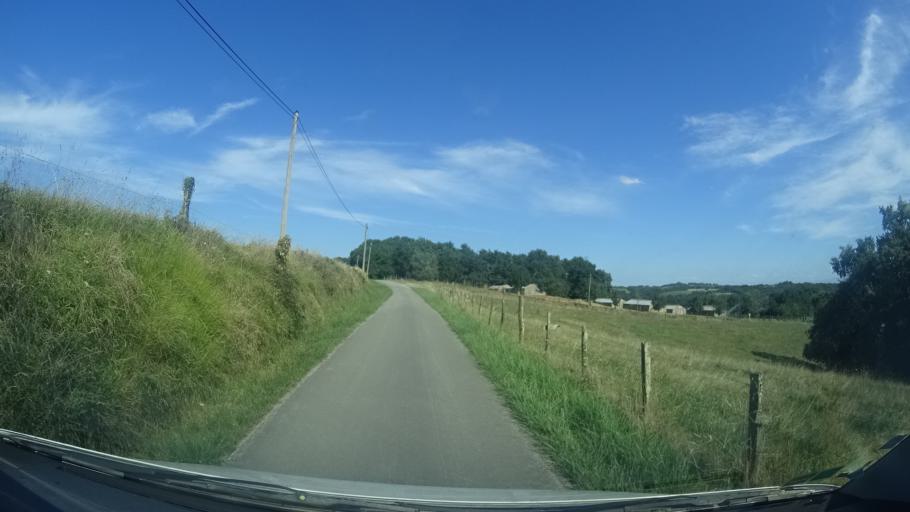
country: FR
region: Aquitaine
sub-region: Departement des Pyrenees-Atlantiques
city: Orthez
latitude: 43.5070
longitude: -0.6999
